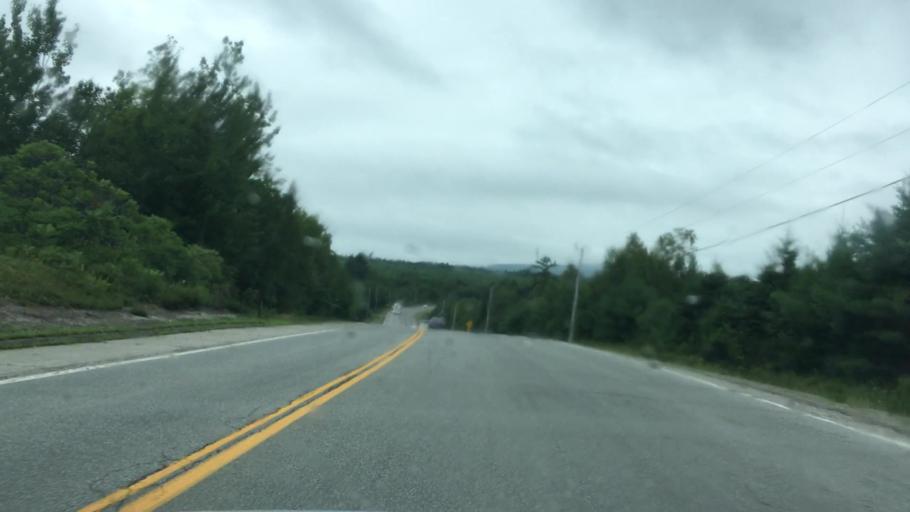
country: US
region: Maine
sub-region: Washington County
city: Cherryfield
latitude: 44.8488
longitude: -68.0613
